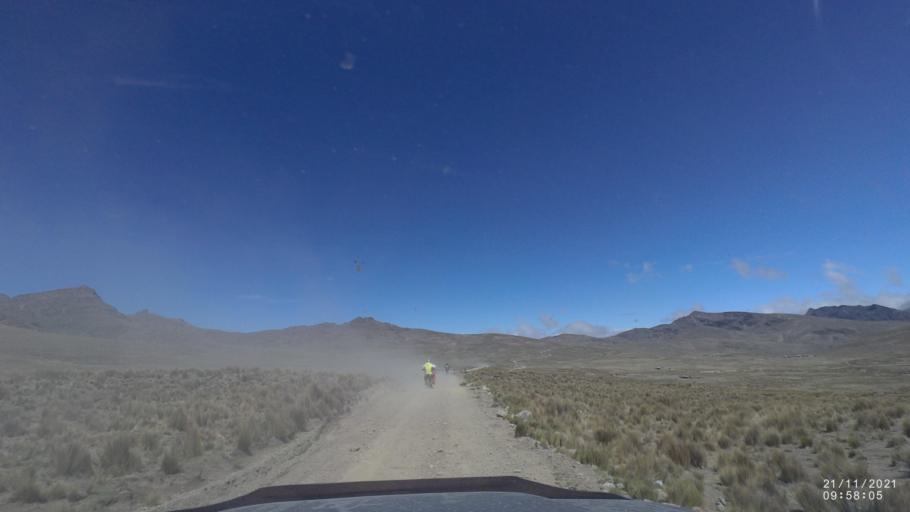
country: BO
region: Cochabamba
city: Cochabamba
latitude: -17.0374
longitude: -66.2748
